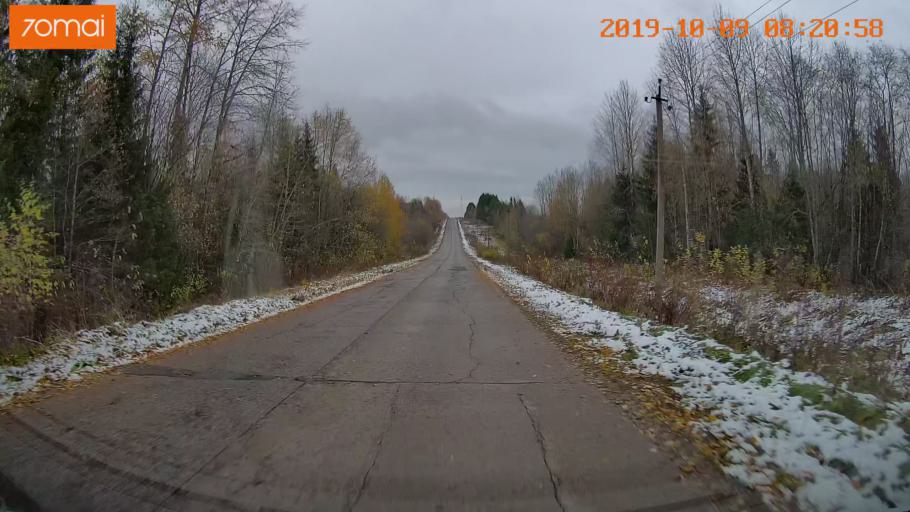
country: RU
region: Vologda
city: Gryazovets
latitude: 58.7424
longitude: 40.2687
